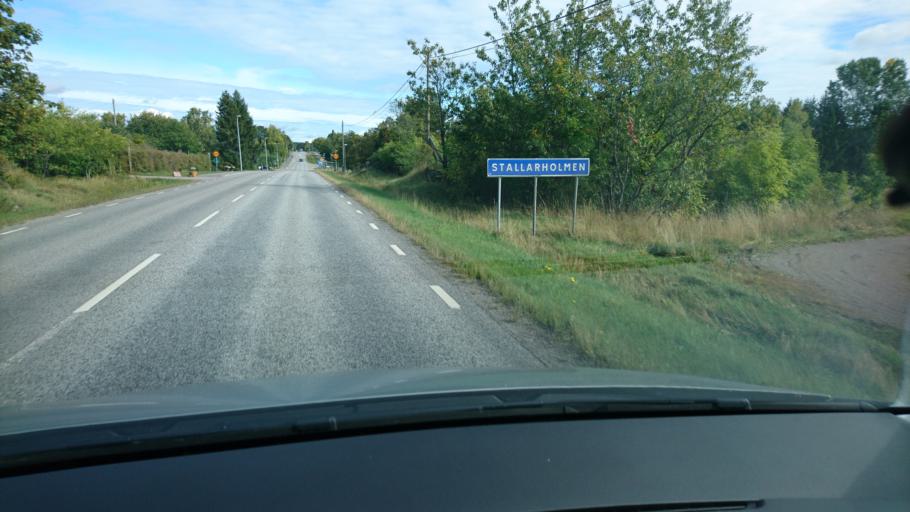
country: SE
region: Soedermanland
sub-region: Strangnas Kommun
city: Stallarholmen
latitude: 59.3534
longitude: 17.1966
